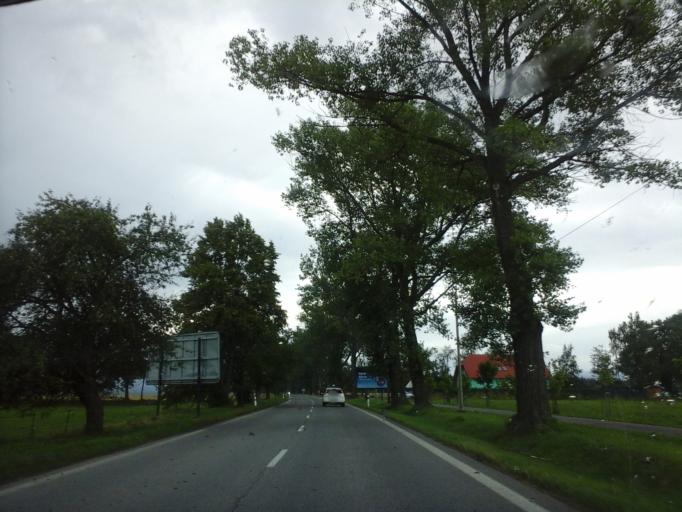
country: SK
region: Presovsky
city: Spisska Bela
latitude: 49.1944
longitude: 20.4414
